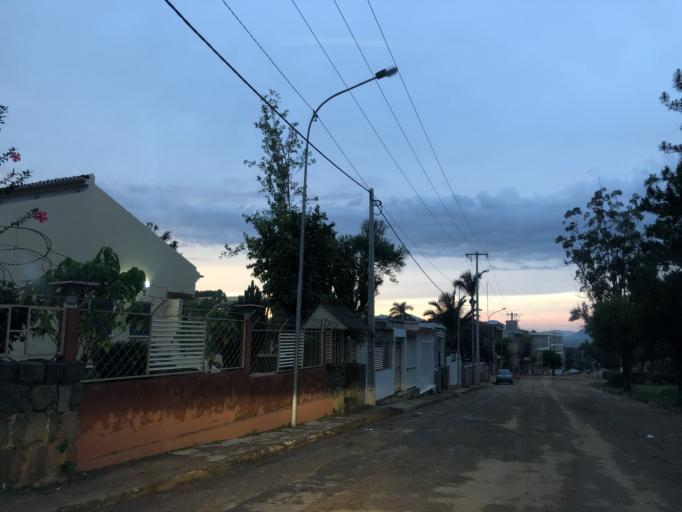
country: AO
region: Cuanza Sul
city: Uacu Cungo
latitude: -11.3661
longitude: 15.1171
